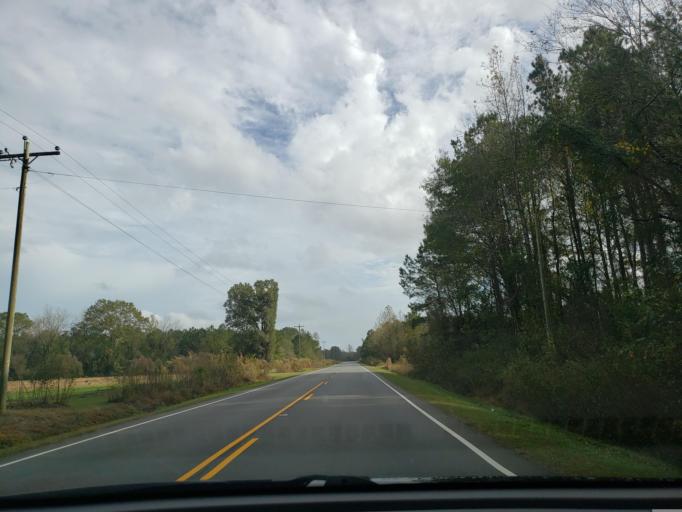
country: US
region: North Carolina
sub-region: Duplin County
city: Beulaville
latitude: 34.8285
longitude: -77.8466
